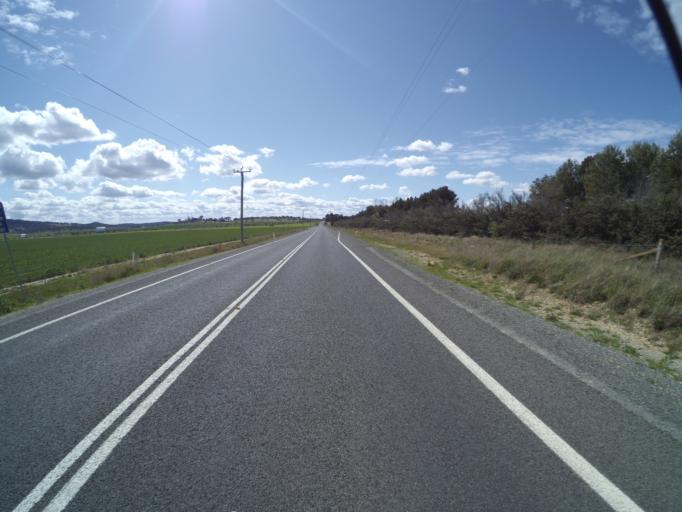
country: AU
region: New South Wales
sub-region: Goulburn Mulwaree
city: Goulburn
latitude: -34.8429
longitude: 149.6832
